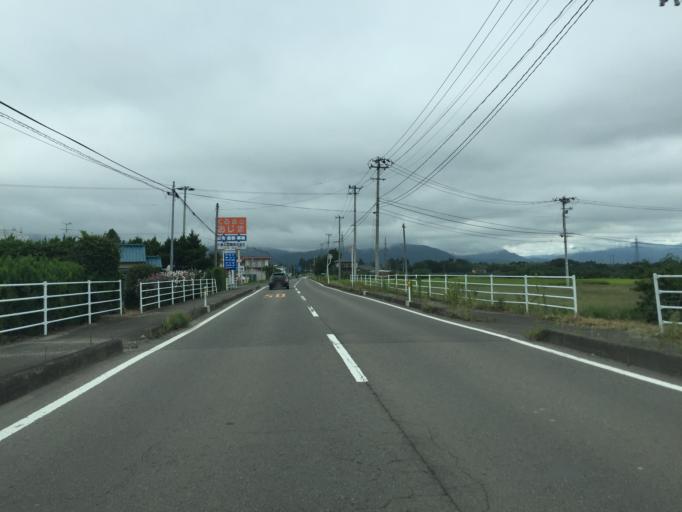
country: JP
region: Fukushima
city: Fukushima-shi
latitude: 37.7498
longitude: 140.4024
